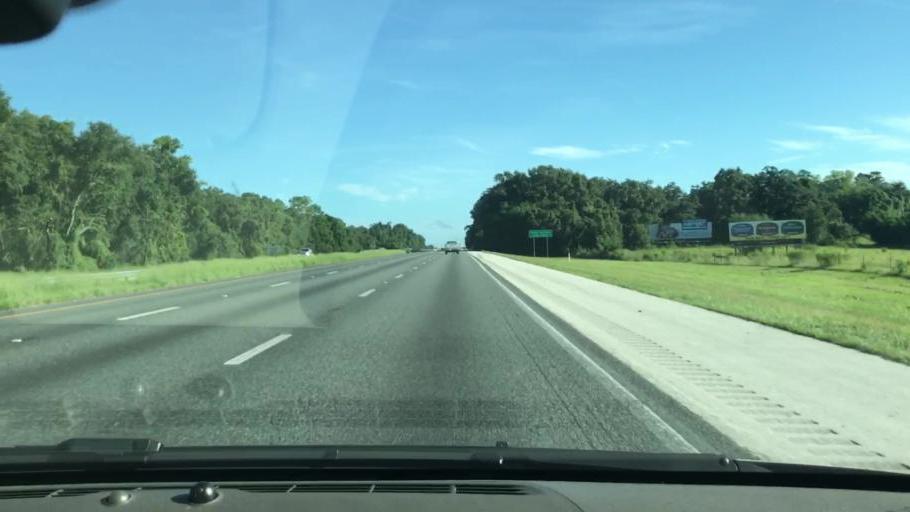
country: US
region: Florida
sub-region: Marion County
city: Ocala
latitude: 29.1097
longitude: -82.1844
